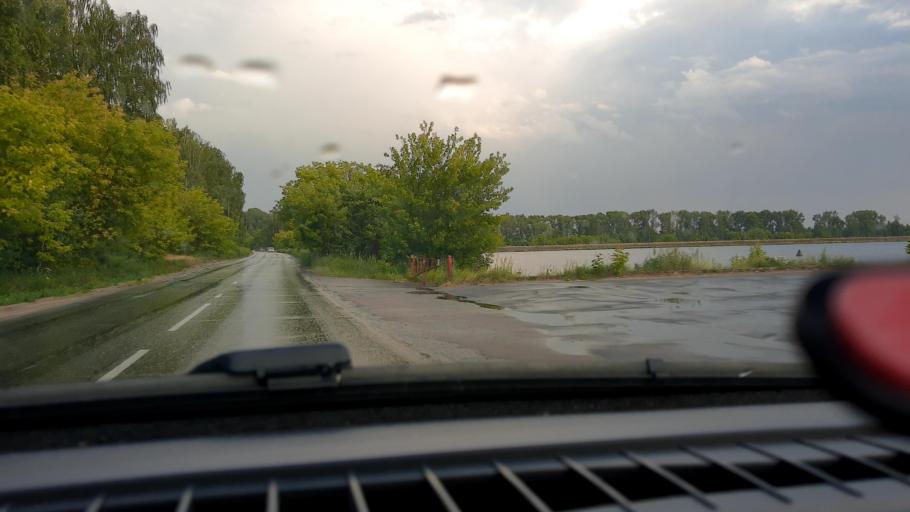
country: RU
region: Nizjnij Novgorod
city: Gorodets
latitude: 56.6713
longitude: 43.4491
